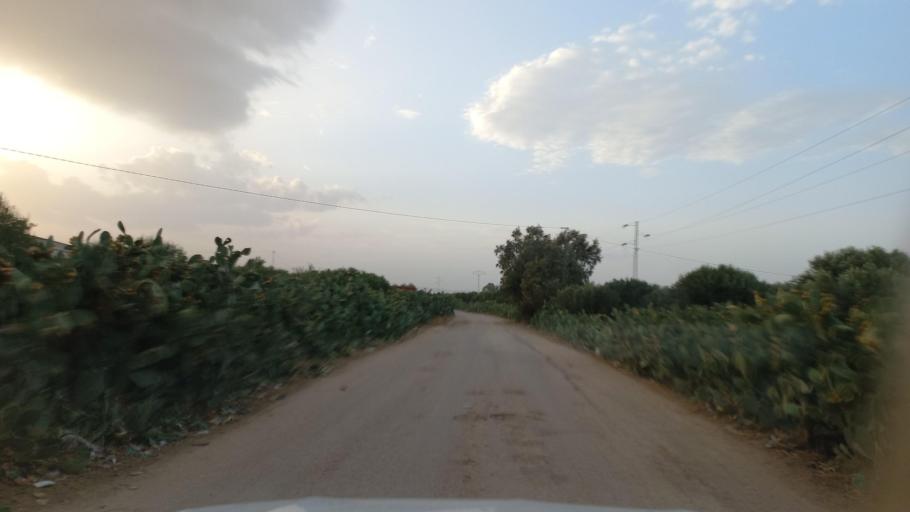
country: TN
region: Al Qasrayn
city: Kasserine
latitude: 35.2678
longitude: 9.0593
